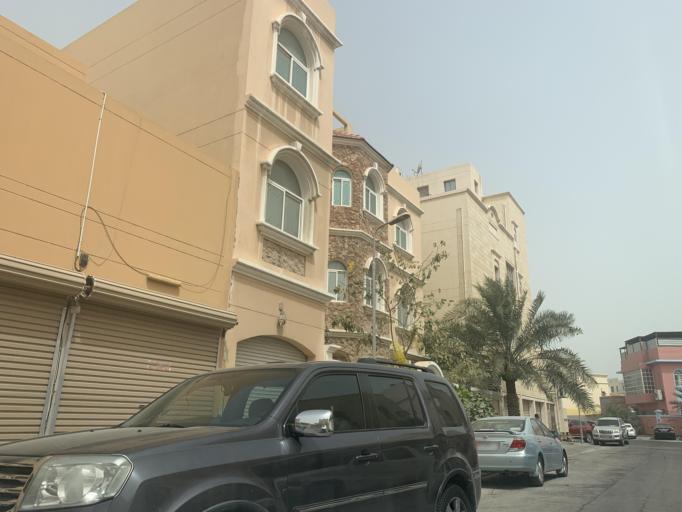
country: BH
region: Manama
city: Jidd Hafs
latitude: 26.2321
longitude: 50.5325
